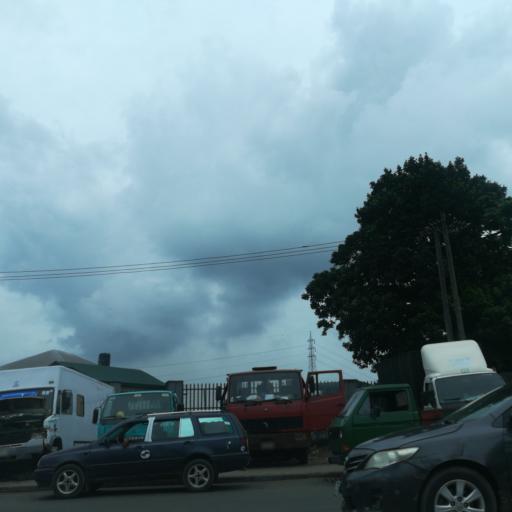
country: NG
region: Rivers
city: Port Harcourt
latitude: 4.8361
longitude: 7.0342
